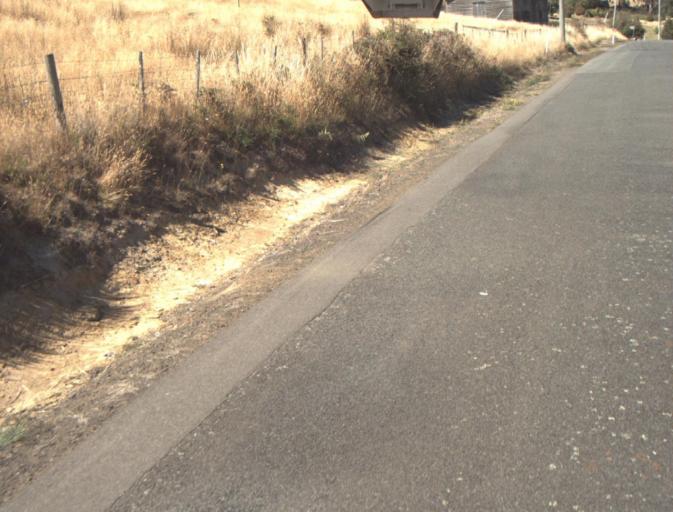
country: AU
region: Tasmania
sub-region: Launceston
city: Newstead
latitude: -41.3522
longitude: 147.3038
